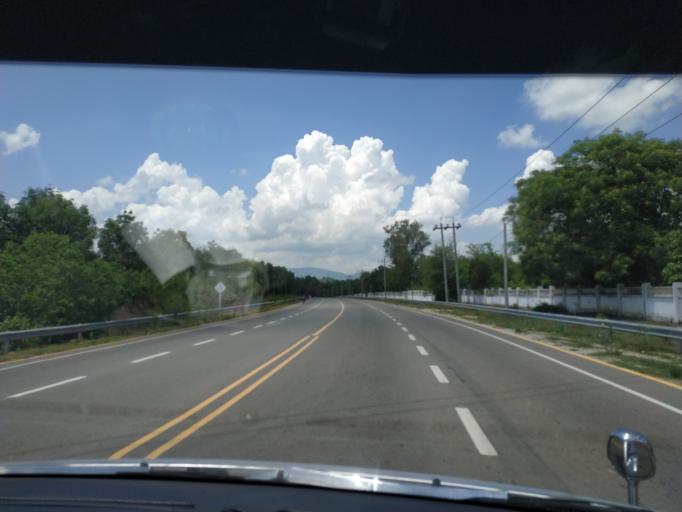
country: MM
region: Mon
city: Kyaikto
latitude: 17.3335
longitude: 97.0370
